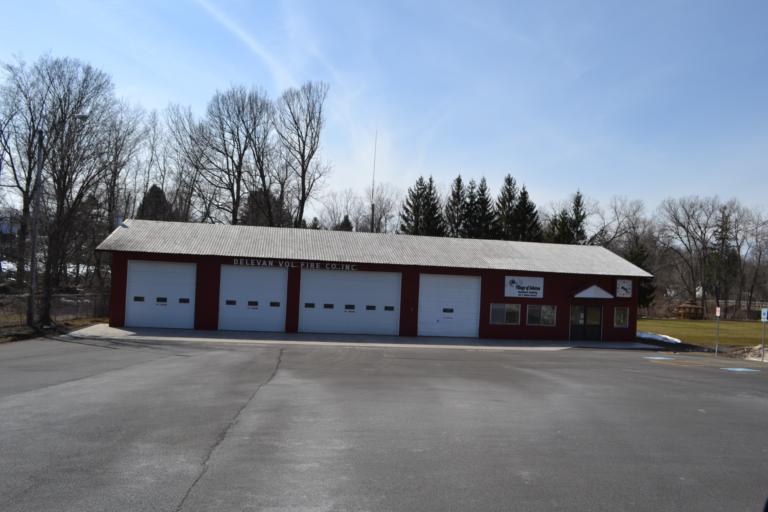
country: US
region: New York
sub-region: Cattaraugus County
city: Delevan
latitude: 42.4882
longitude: -78.4805
